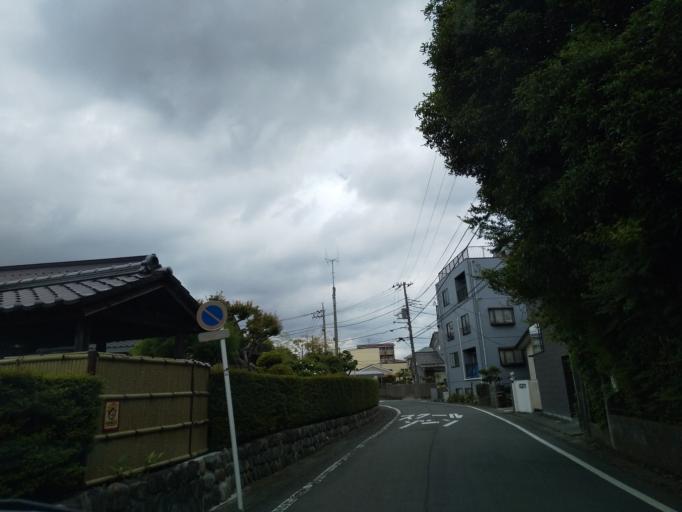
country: JP
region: Kanagawa
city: Zama
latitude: 35.5539
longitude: 139.3620
